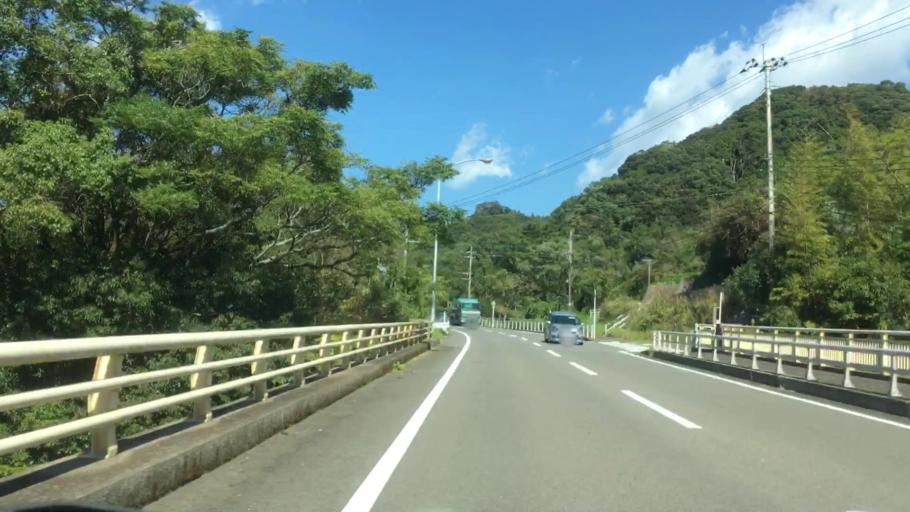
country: JP
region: Nagasaki
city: Sasebo
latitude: 33.0012
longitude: 129.6618
